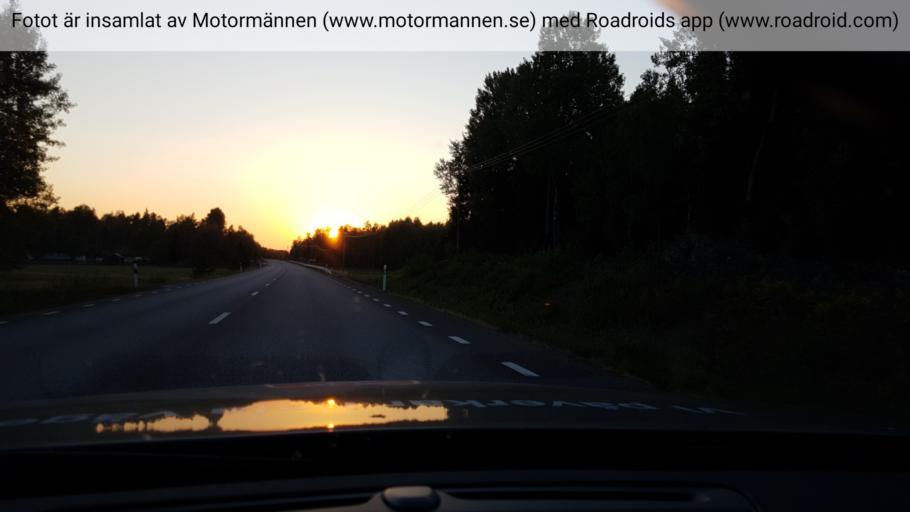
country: SE
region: Uppsala
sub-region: Osthammars Kommun
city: Bjorklinge
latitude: 59.9680
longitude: 17.3771
